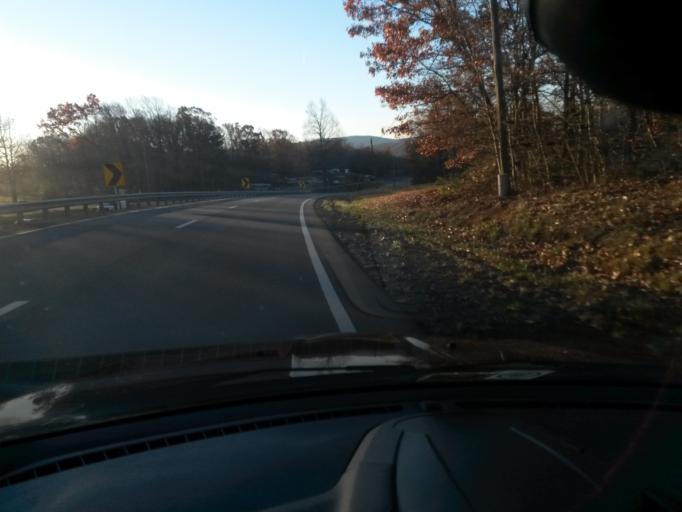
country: US
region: Virginia
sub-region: Franklin County
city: Henry Fork
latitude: 36.9253
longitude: -79.8661
